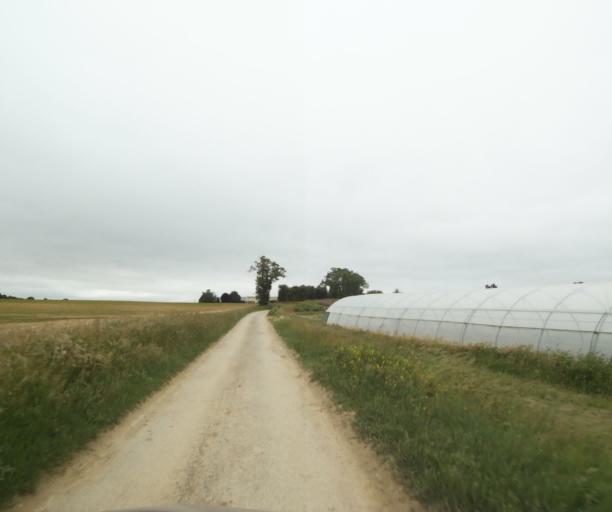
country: FR
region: Rhone-Alpes
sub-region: Departement du Rhone
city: Rillieux-la-Pape
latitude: 45.8488
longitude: 4.9134
